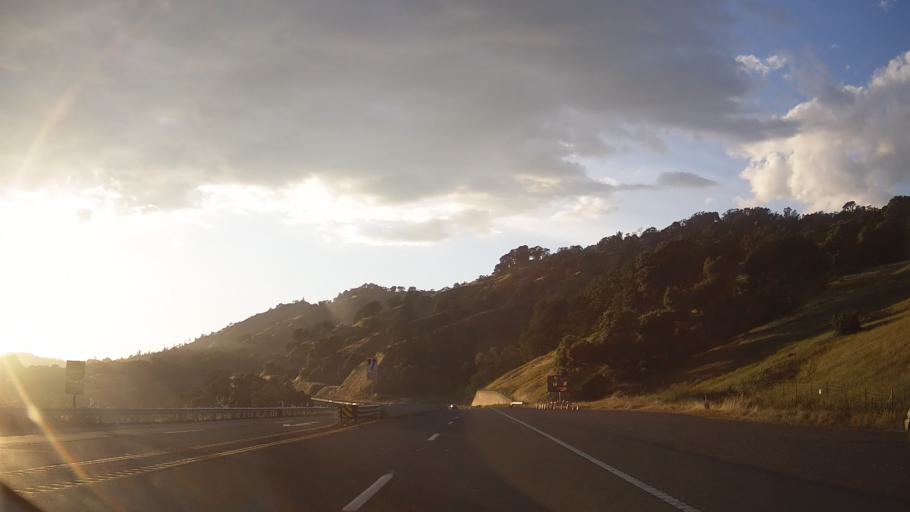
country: US
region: California
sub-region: Mendocino County
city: Redwood Valley
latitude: 39.2867
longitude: -123.2631
